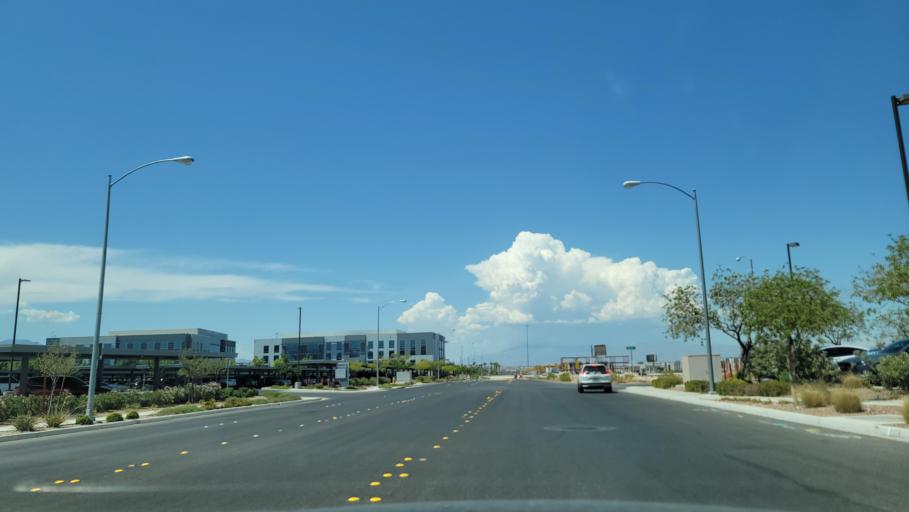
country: US
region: Nevada
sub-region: Clark County
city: Enterprise
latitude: 36.0624
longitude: -115.2701
